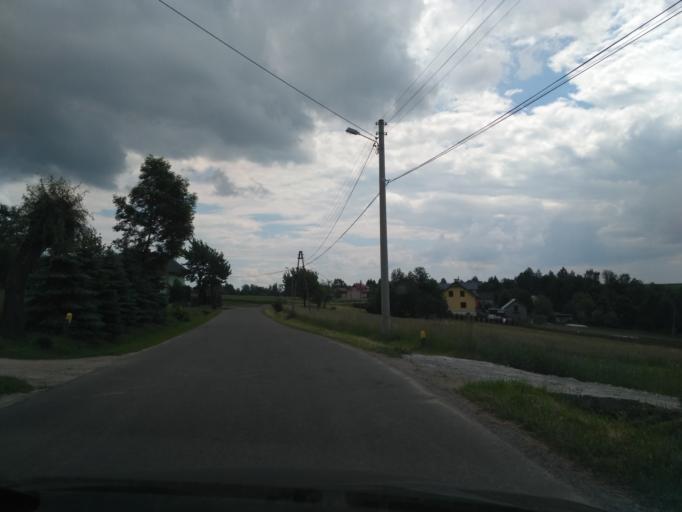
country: PL
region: Subcarpathian Voivodeship
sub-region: Powiat rzeszowski
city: Hyzne
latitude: 49.9342
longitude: 22.1814
